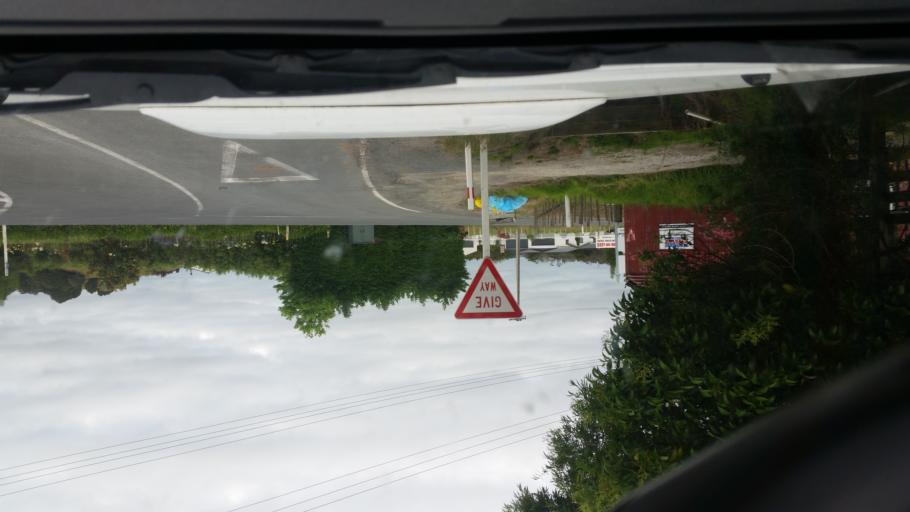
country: NZ
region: Northland
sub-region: Kaipara District
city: Dargaville
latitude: -35.9236
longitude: 173.8927
